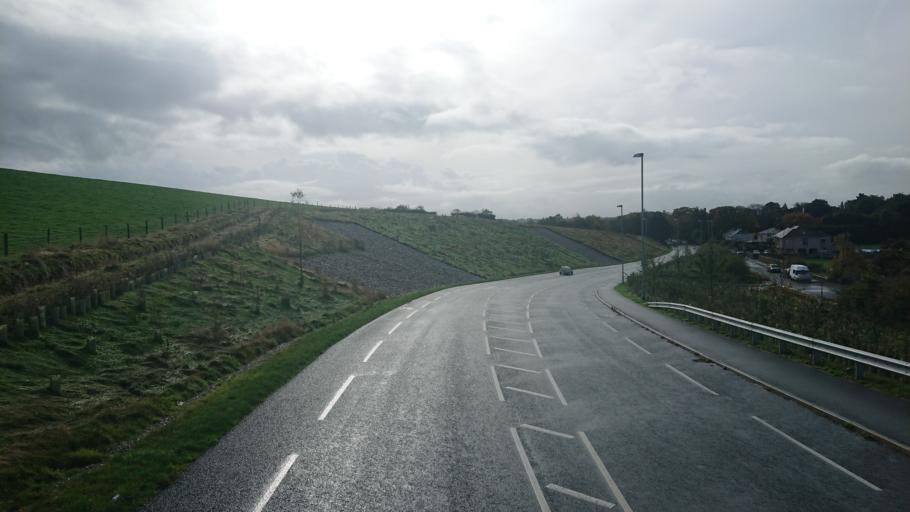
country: GB
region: England
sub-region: Lancashire
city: Bolton le Sands
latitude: 54.0715
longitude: -2.8007
